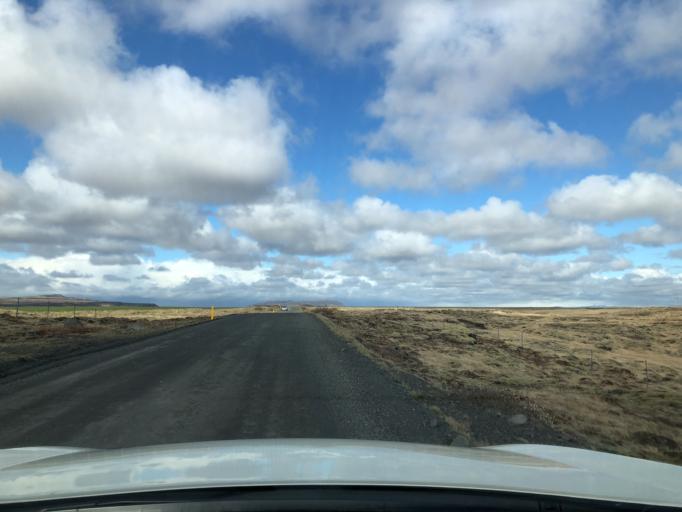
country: IS
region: South
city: Selfoss
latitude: 63.9289
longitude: -20.6717
